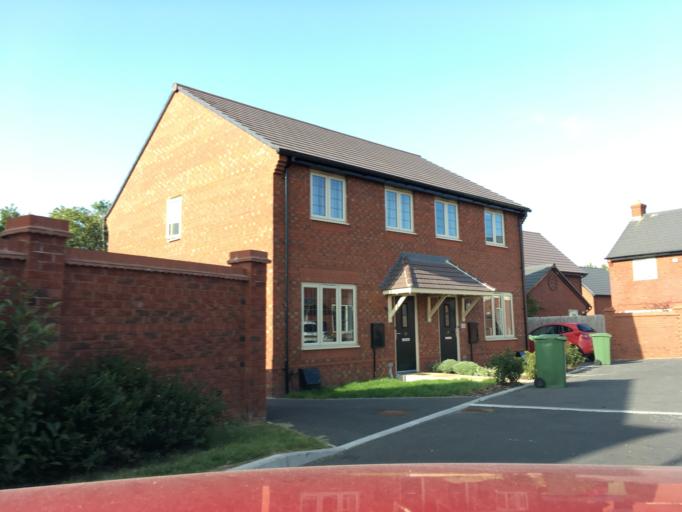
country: GB
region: England
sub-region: Gloucestershire
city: Tewkesbury
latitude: 51.9786
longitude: -2.1452
